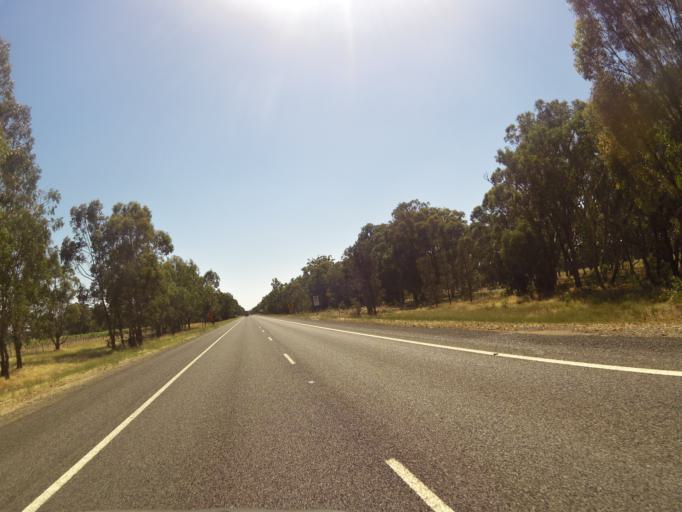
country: AU
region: Victoria
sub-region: Greater Shepparton
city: Shepparton
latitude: -36.8025
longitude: 145.4692
